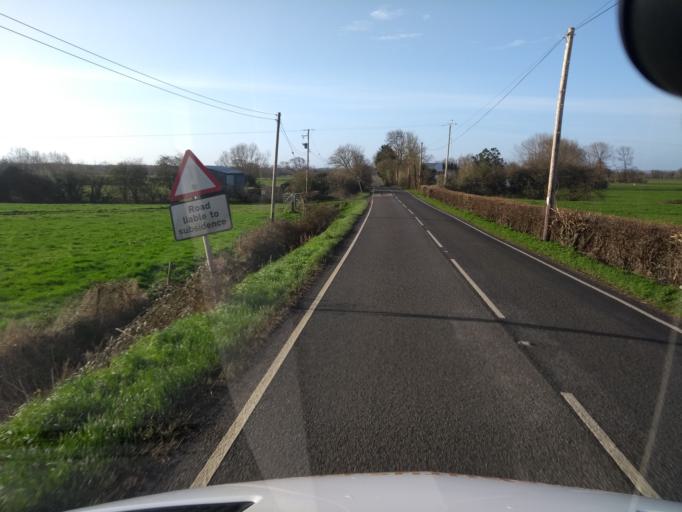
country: GB
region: England
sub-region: Somerset
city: Wedmore
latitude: 51.2057
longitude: -2.8007
